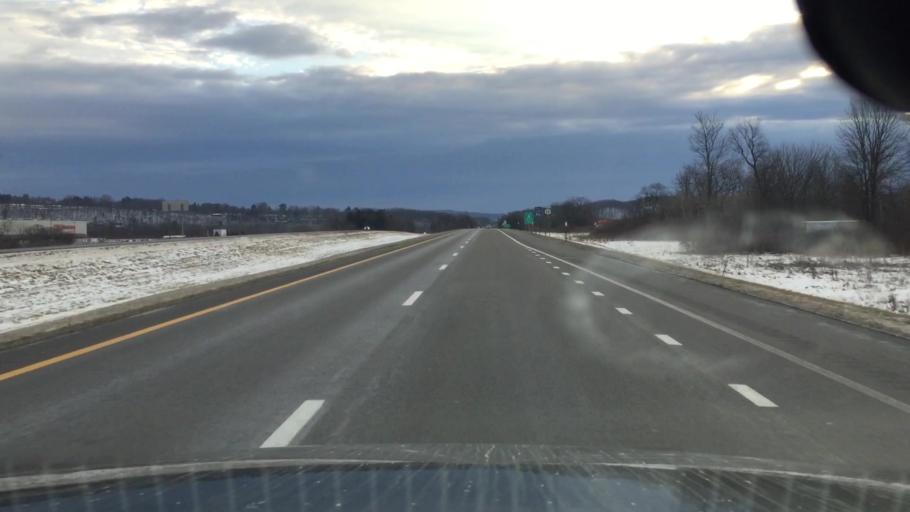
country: US
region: Pennsylvania
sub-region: Bradford County
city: South Waverly
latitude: 42.0007
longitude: -76.5801
